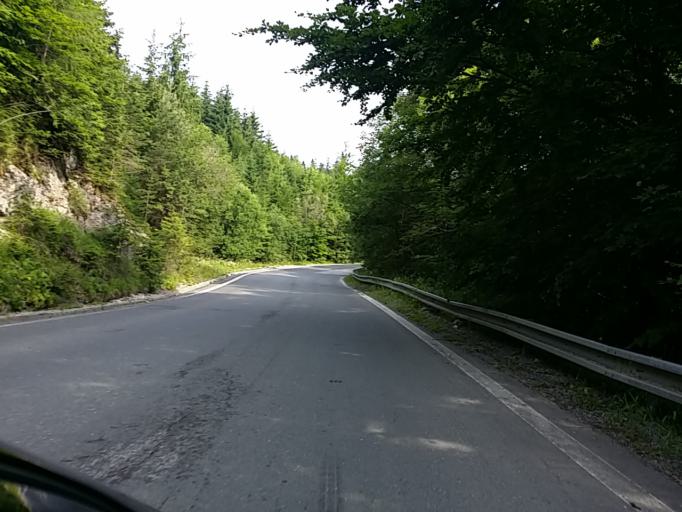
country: SK
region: Kosicky
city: Dobsina
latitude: 48.8973
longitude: 20.2467
